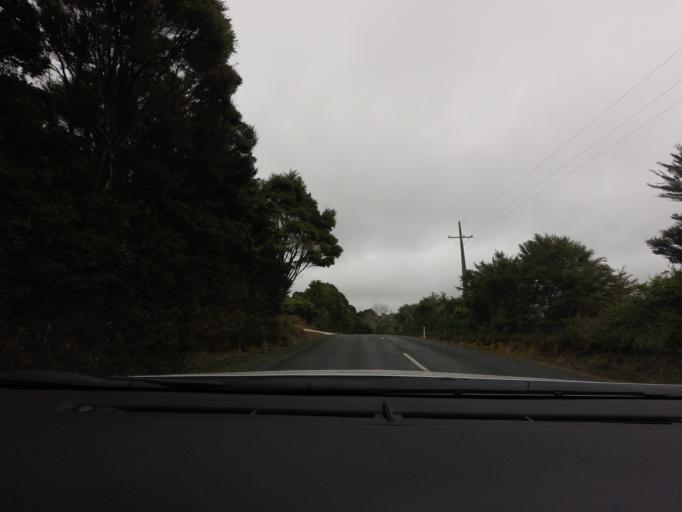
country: NZ
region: Auckland
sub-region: Auckland
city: Wellsford
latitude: -36.2816
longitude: 174.6019
